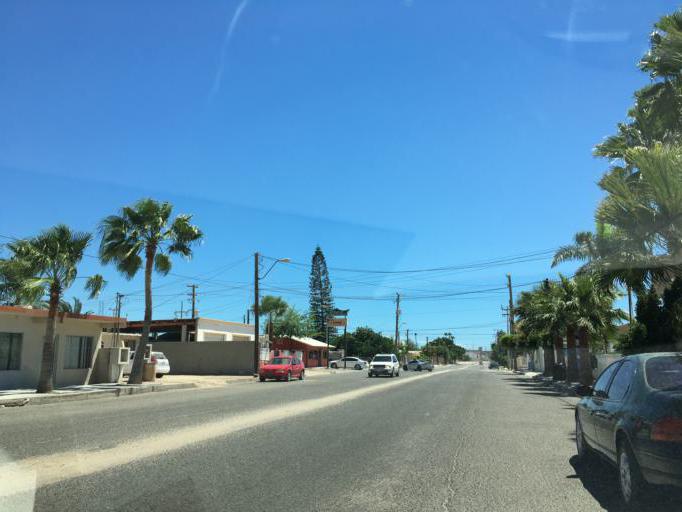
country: MX
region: Sonora
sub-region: Puerto Penasco
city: Puerto Penasco
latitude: 31.3107
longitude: -113.5337
